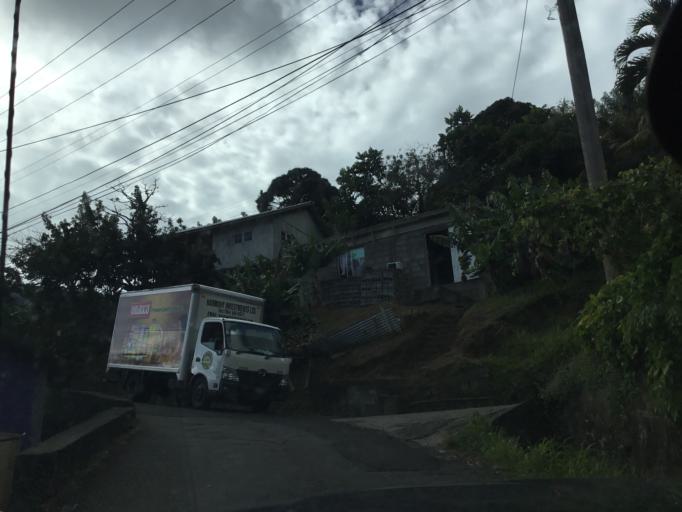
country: VC
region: Saint George
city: Kingstown
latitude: 13.1638
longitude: -61.2179
